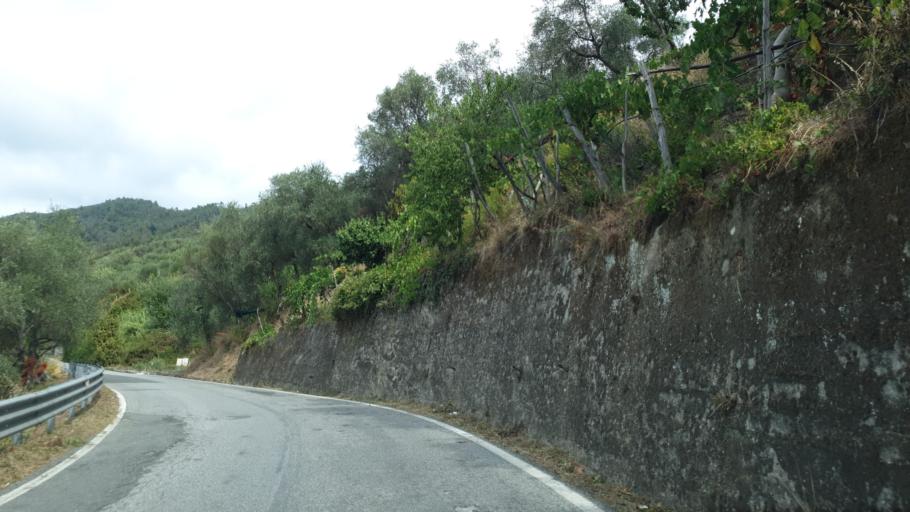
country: IT
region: Liguria
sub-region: Provincia di La Spezia
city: Levanto
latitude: 44.1920
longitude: 9.6287
